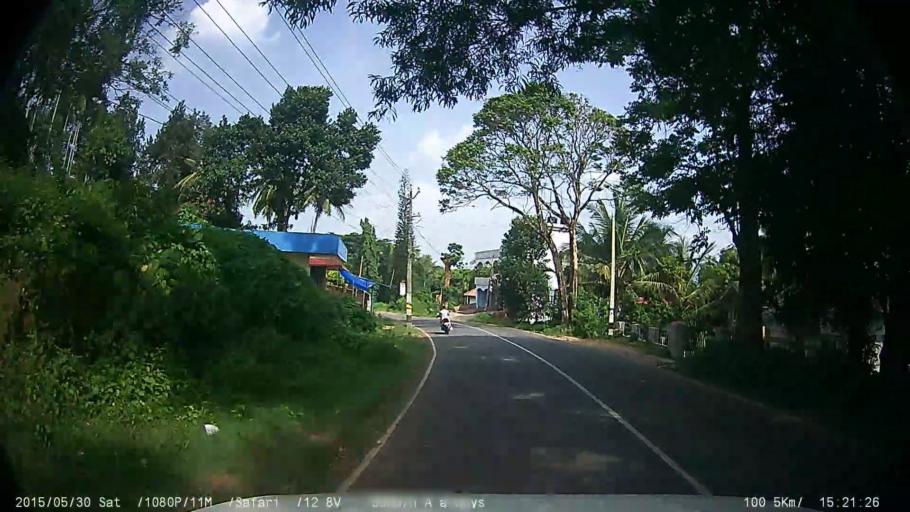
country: IN
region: Kerala
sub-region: Wayanad
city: Panamaram
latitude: 11.7481
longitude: 76.0685
